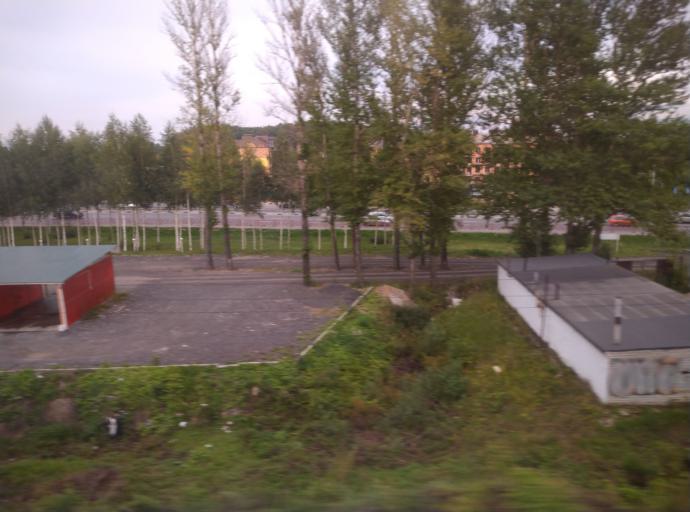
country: RU
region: Jaroslavl
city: Yaroslavl
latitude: 57.5963
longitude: 39.8926
